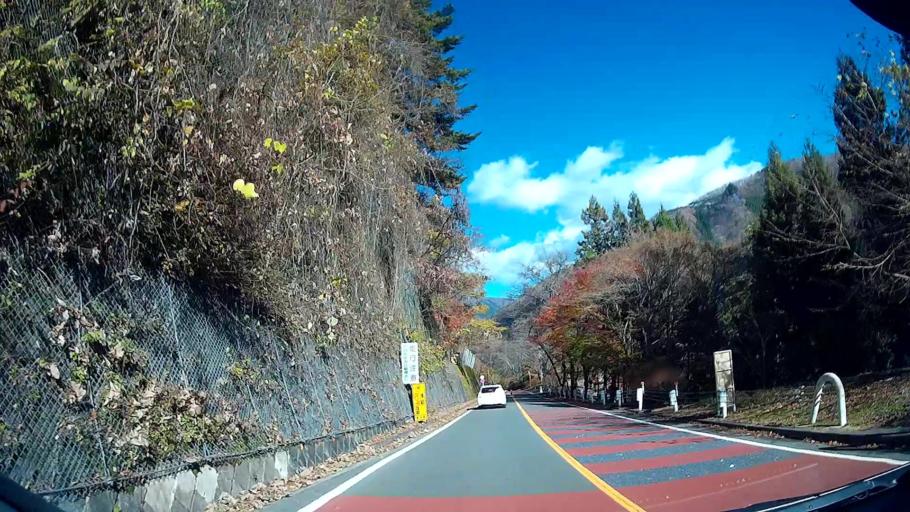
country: JP
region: Yamanashi
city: Uenohara
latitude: 35.7588
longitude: 139.0235
